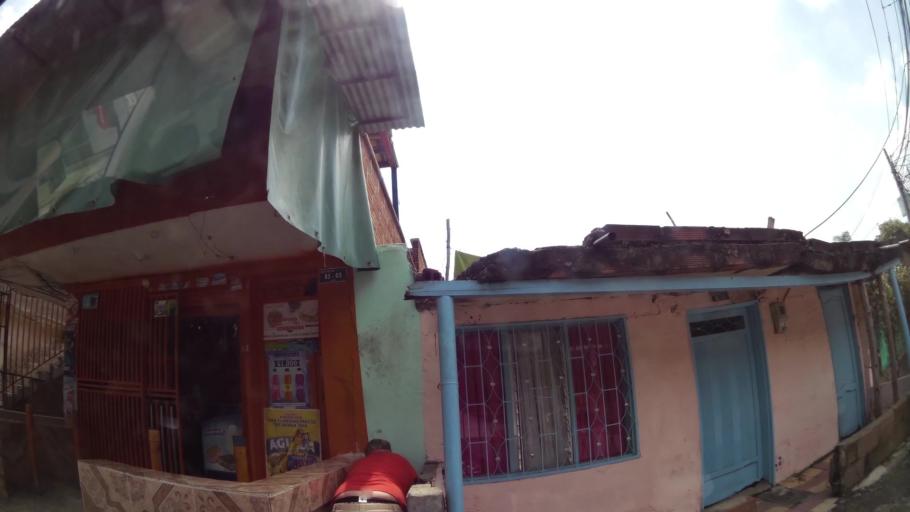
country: CO
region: Antioquia
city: La Estrella
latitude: 6.1815
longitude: -75.6614
